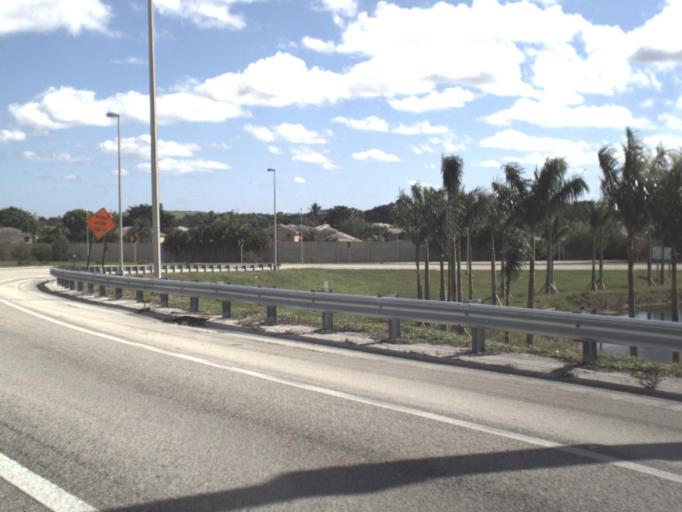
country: US
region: Florida
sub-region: Broward County
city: Parkland
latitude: 26.2999
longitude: -80.2007
